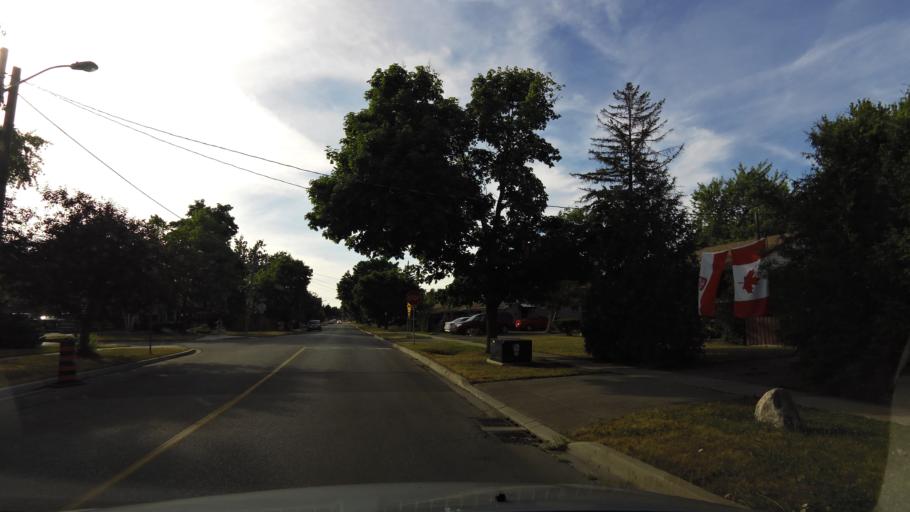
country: CA
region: Ontario
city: Brampton
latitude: 43.6865
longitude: -79.7401
